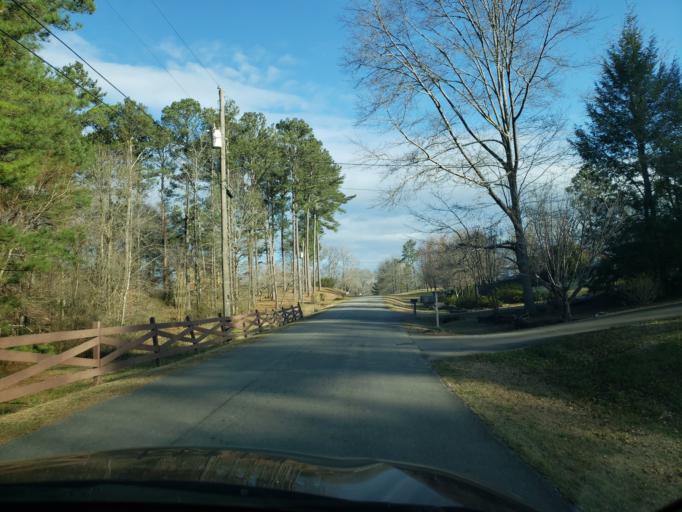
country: US
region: Alabama
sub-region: Cleburne County
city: Heflin
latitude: 33.6365
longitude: -85.6009
